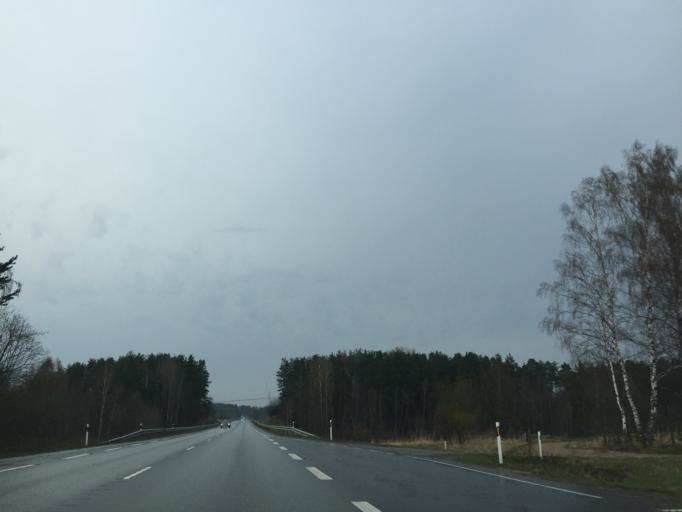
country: EE
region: Tartu
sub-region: UElenurme vald
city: Ulenurme
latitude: 58.2112
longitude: 26.7063
